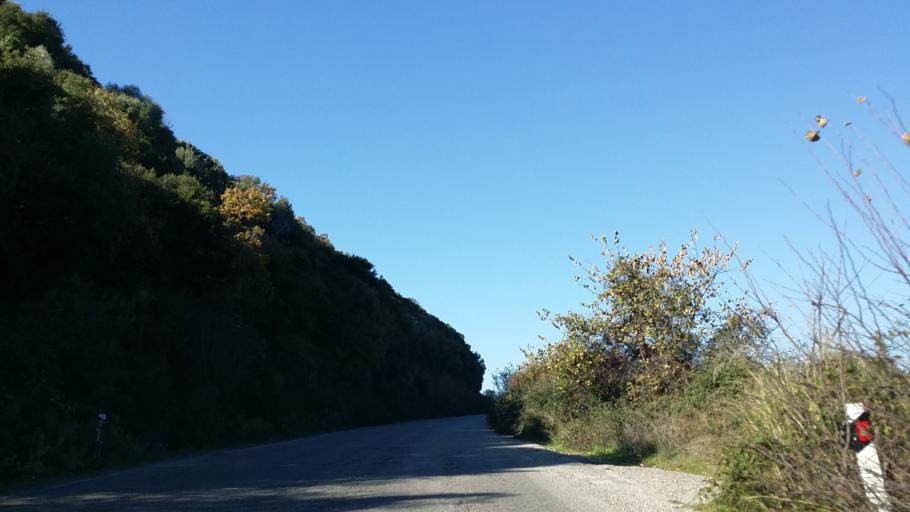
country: GR
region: West Greece
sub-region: Nomos Aitolias kai Akarnanias
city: Monastirakion
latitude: 38.8717
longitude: 21.0429
